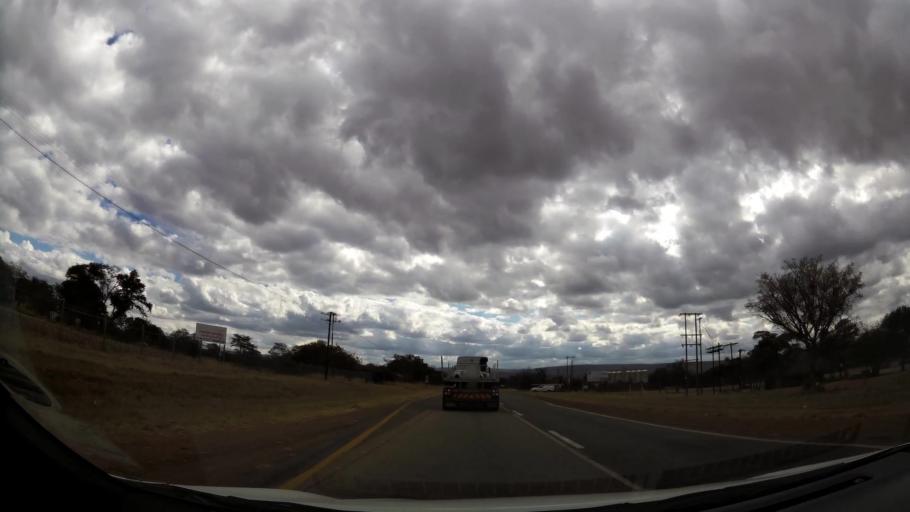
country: ZA
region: Limpopo
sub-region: Waterberg District Municipality
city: Modimolle
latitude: -24.7253
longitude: 28.4267
